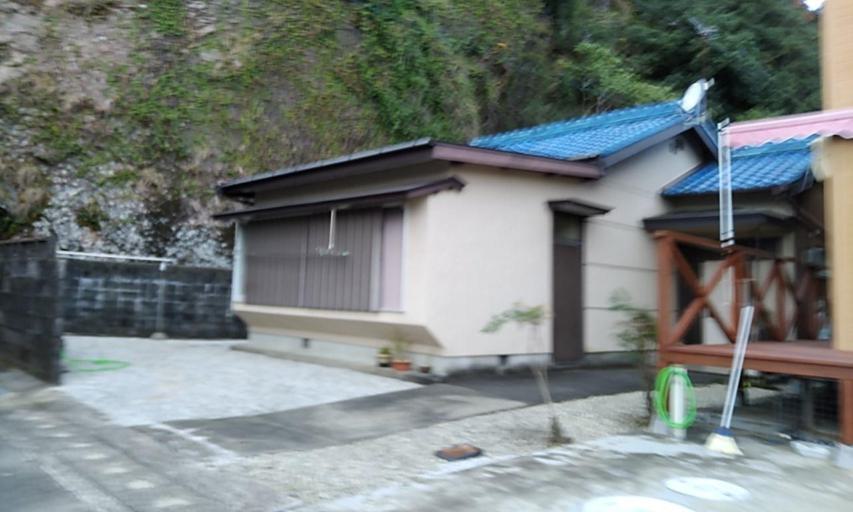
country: JP
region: Wakayama
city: Shingu
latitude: 33.7220
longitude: 135.9836
